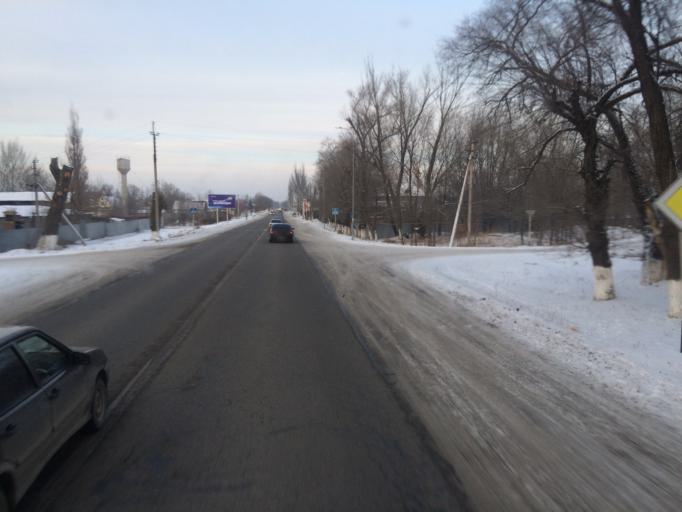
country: KZ
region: Almaty Oblysy
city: Burunday
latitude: 43.2662
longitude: 76.6702
